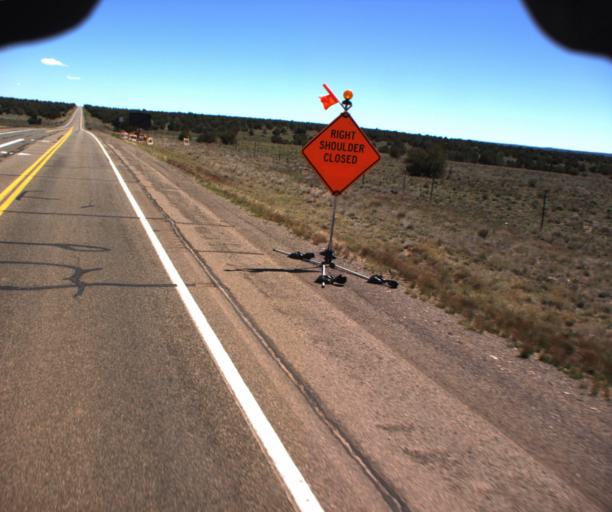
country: US
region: Arizona
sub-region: Coconino County
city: Williams
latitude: 35.1900
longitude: -112.4695
